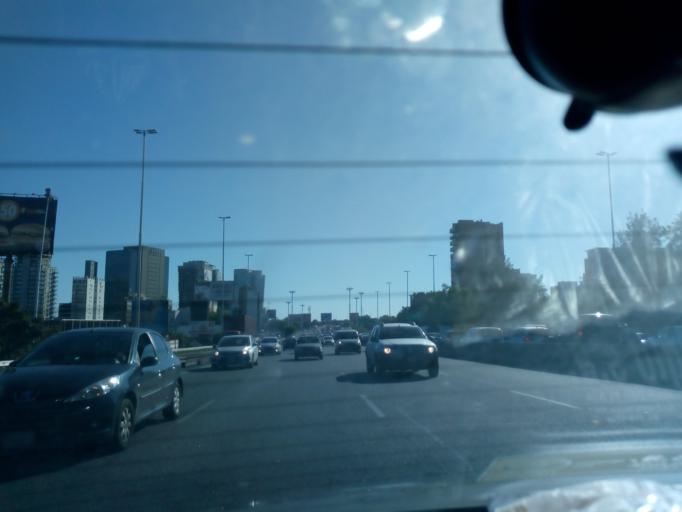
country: AR
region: Buenos Aires
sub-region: Partido de Vicente Lopez
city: Olivos
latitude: -34.5369
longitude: -58.4714
